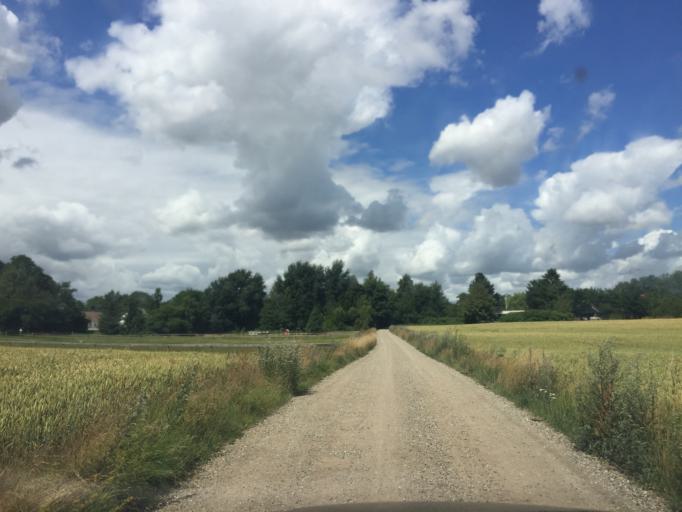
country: DK
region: Capital Region
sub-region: Egedal Kommune
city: Smorumnedre
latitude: 55.7054
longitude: 12.2675
